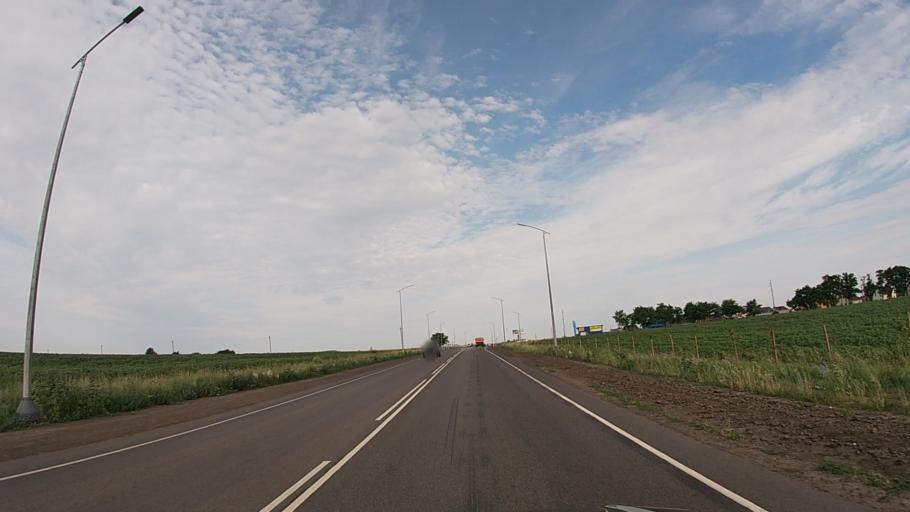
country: RU
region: Belgorod
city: Severnyy
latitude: 50.6650
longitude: 36.5054
